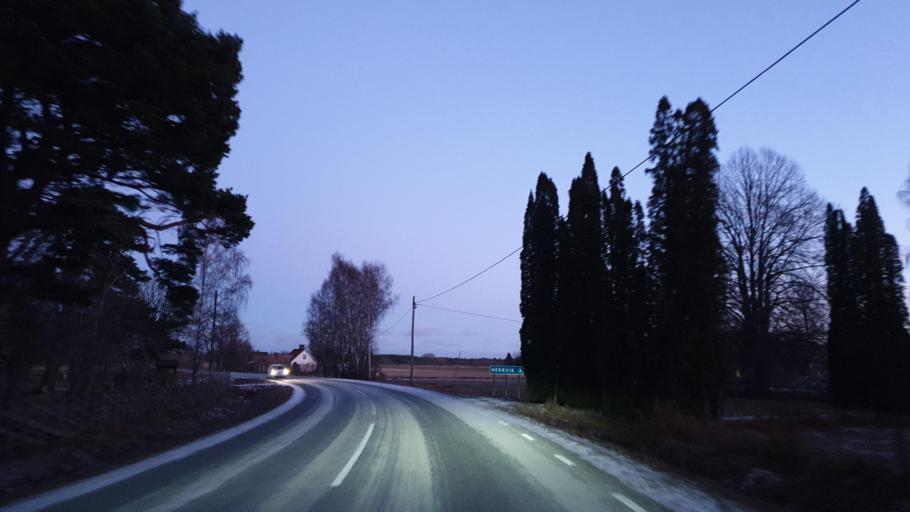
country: SE
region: Gotland
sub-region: Gotland
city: Slite
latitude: 57.4200
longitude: 18.8615
